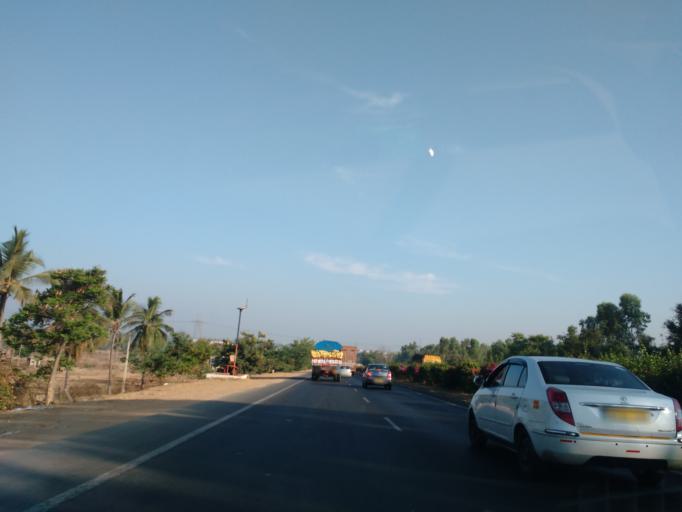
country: IN
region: Karnataka
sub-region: Bangalore Rural
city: Nelamangala
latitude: 13.1223
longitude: 77.3672
